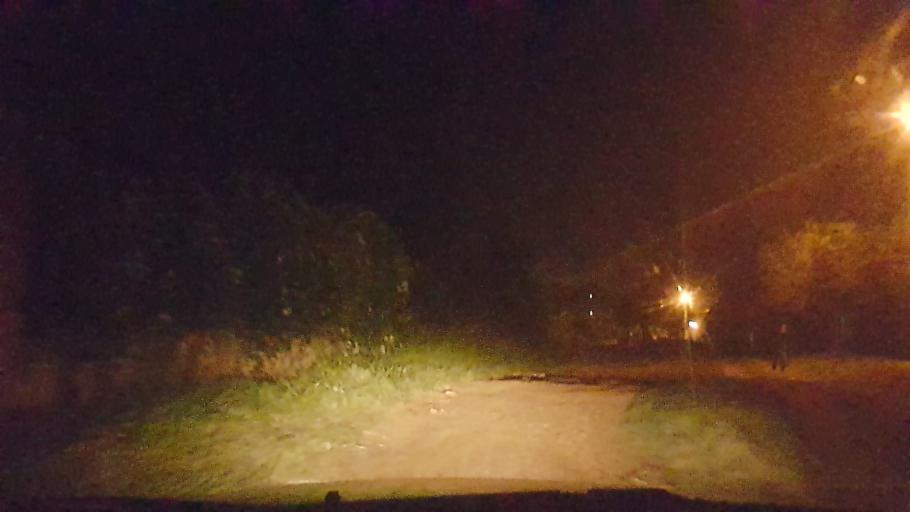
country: PY
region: Central
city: Colonia Mariano Roque Alonso
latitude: -25.1872
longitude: -57.5197
